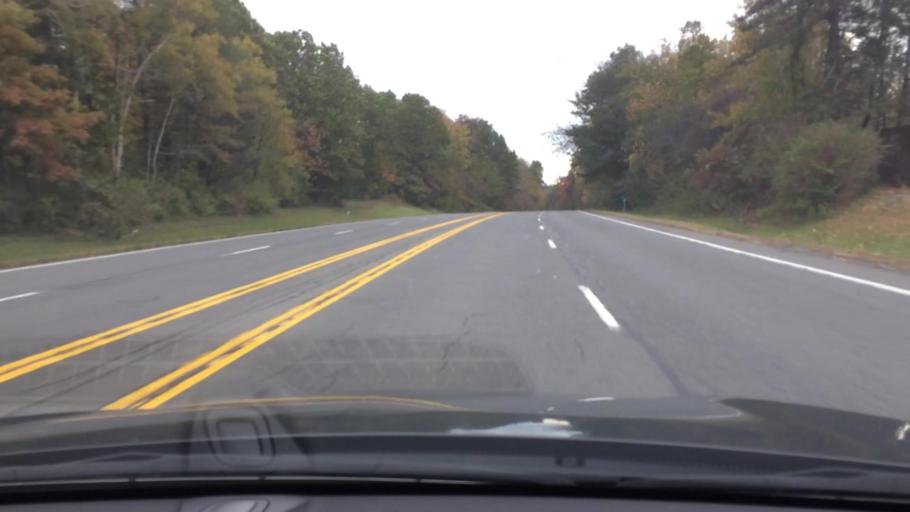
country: US
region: New York
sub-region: Columbia County
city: Valatie
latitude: 42.4204
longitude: -73.6897
